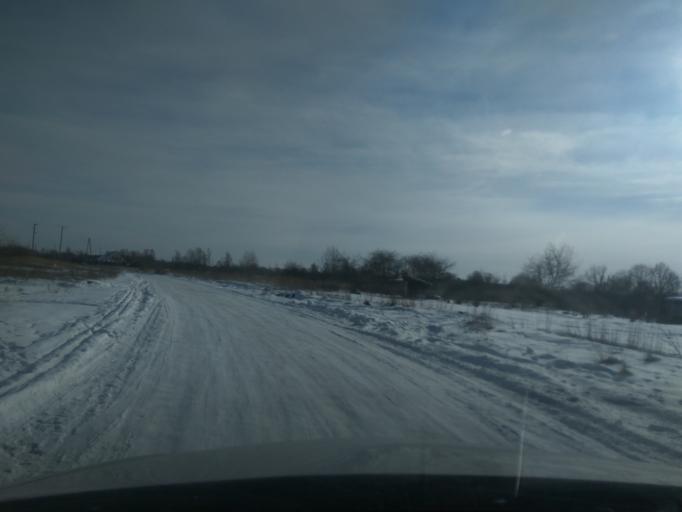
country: LV
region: Kuldigas Rajons
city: Kuldiga
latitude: 56.9839
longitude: 21.9540
